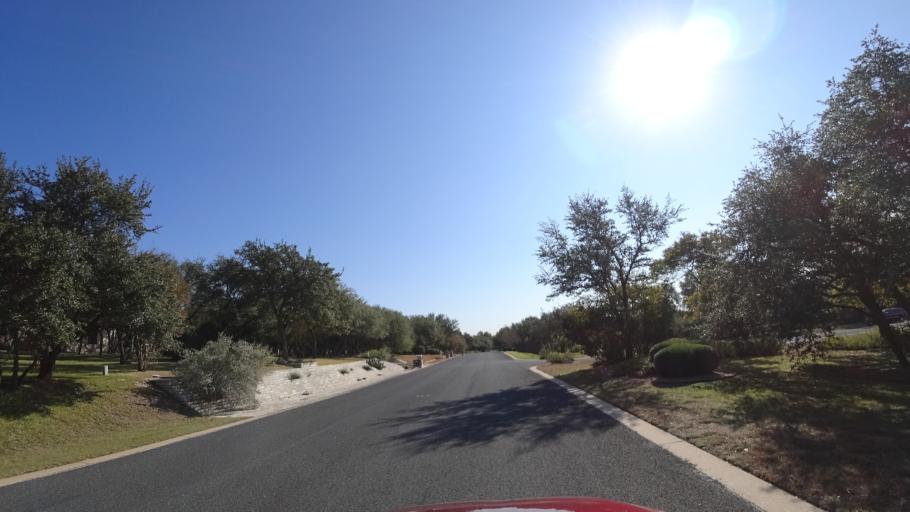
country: US
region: Texas
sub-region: Williamson County
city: Anderson Mill
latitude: 30.3809
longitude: -97.8303
